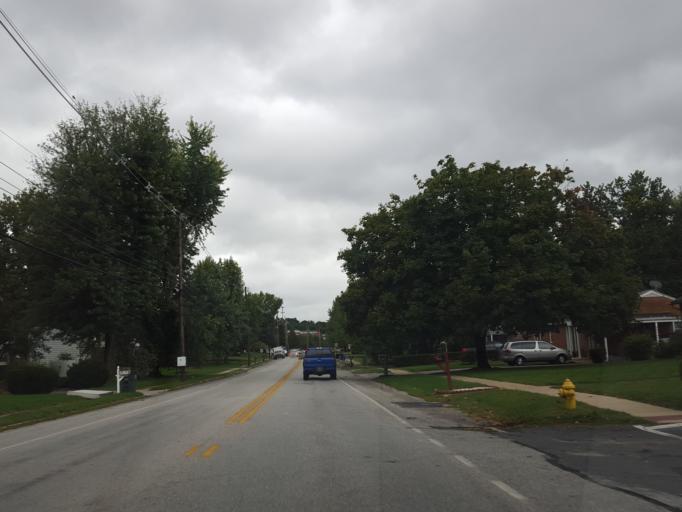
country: US
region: Pennsylvania
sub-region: York County
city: East York
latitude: 39.9640
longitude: -76.6809
